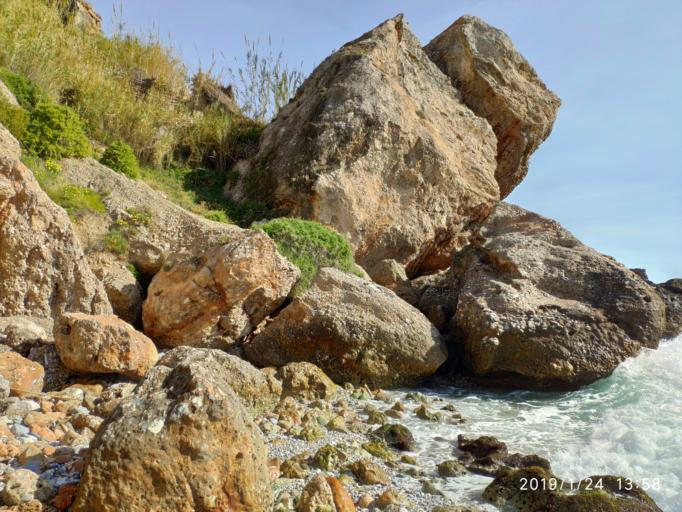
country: ES
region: Andalusia
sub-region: Provincia de Malaga
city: Nerja
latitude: 36.7512
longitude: -3.8507
